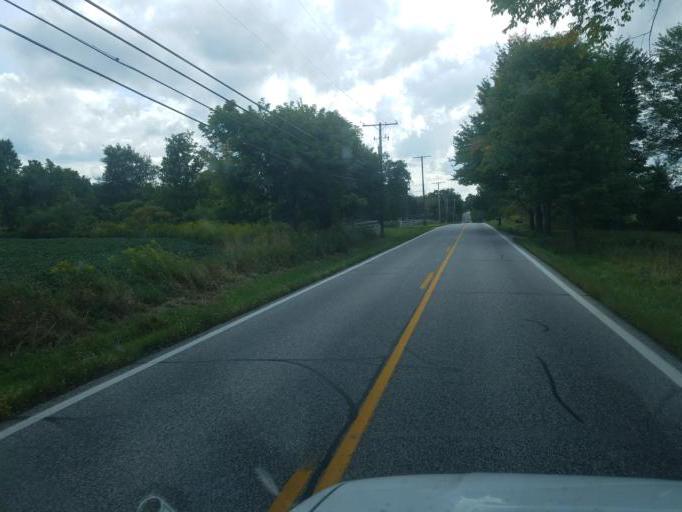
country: US
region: Ohio
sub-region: Geauga County
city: Burton
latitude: 41.4409
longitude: -81.1377
